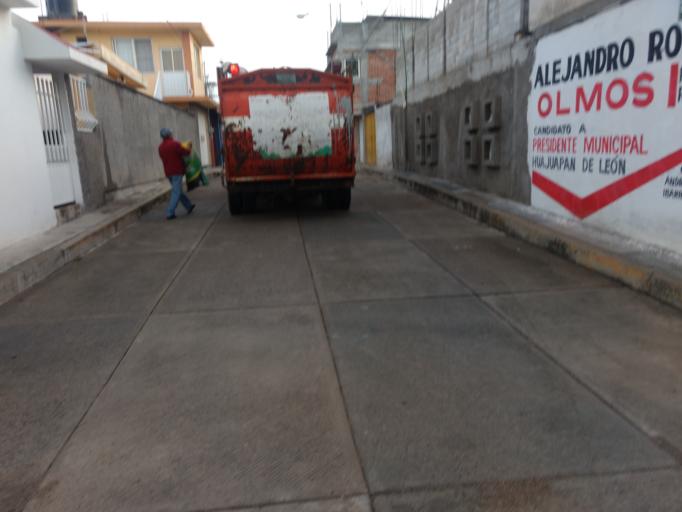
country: MX
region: Oaxaca
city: Ciudad de Huajuapam de Leon
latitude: 17.8096
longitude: -97.7811
